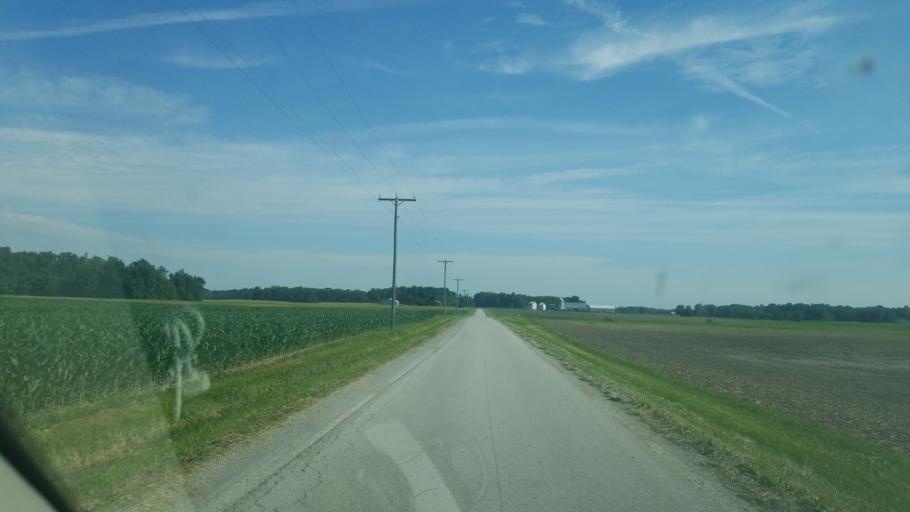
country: US
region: Ohio
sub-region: Wyandot County
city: Upper Sandusky
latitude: 40.8578
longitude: -83.2370
